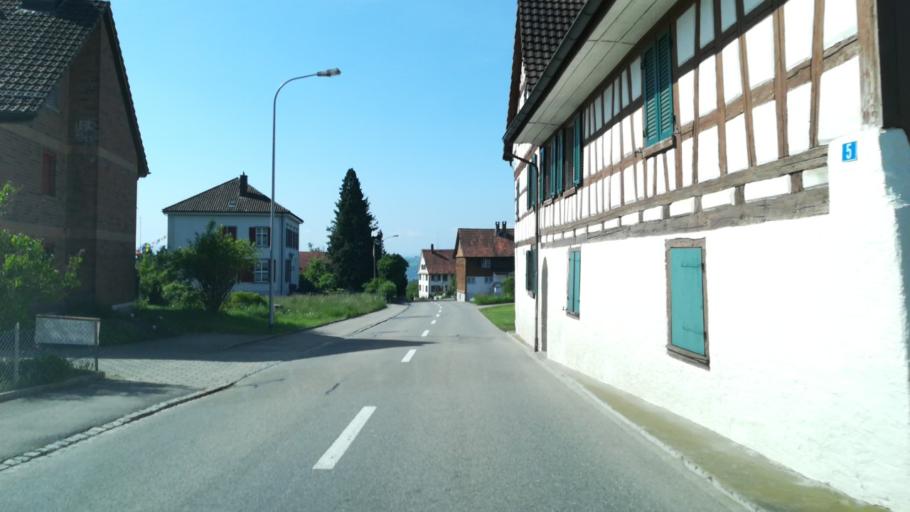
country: CH
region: Thurgau
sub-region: Weinfelden District
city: Wigoltingen
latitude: 47.6197
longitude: 9.0383
